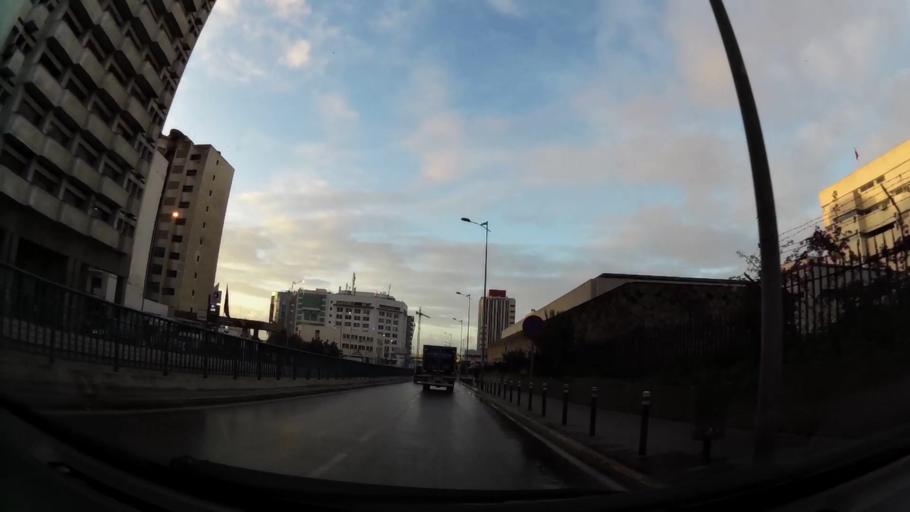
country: MA
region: Grand Casablanca
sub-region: Casablanca
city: Casablanca
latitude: 33.5944
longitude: -7.6034
